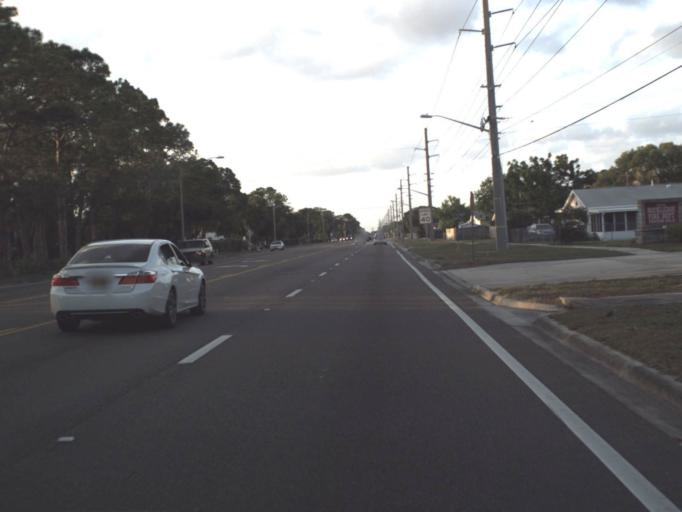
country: US
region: Florida
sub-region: Brevard County
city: Rockledge
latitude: 28.3323
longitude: -80.7425
